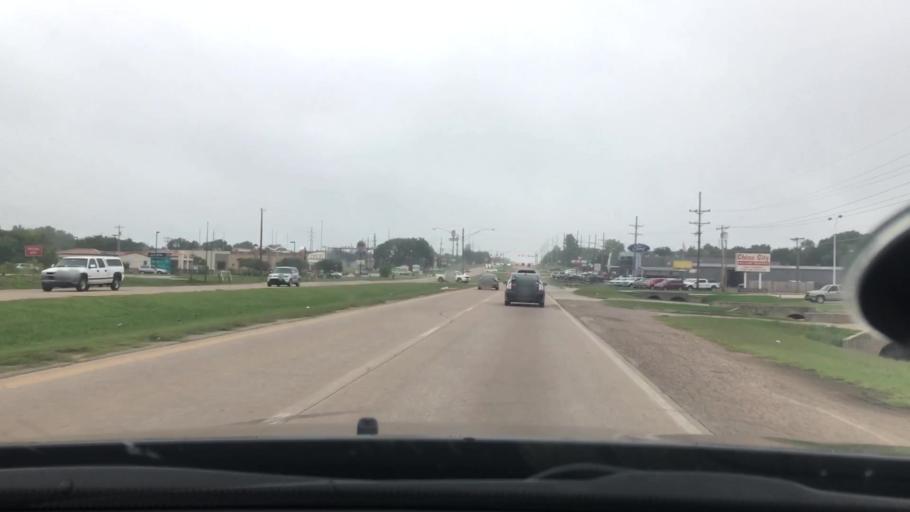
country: US
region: Oklahoma
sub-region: Seminole County
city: Seminole
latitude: 35.2416
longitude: -96.6709
